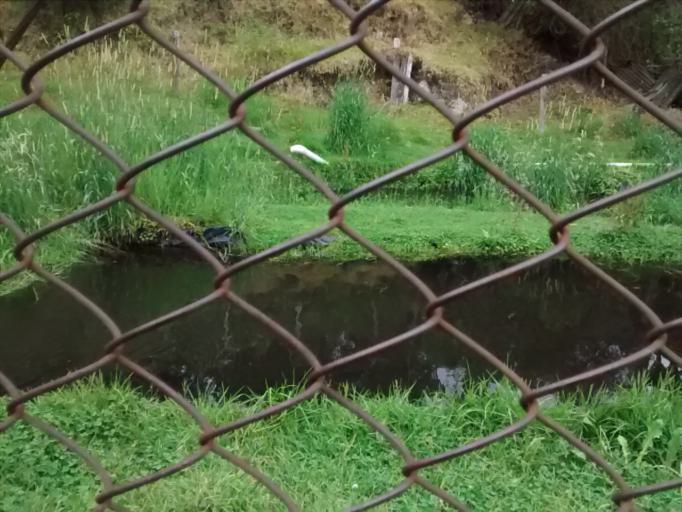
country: CO
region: Bogota D.C.
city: Bogota
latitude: 4.5593
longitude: -74.0634
